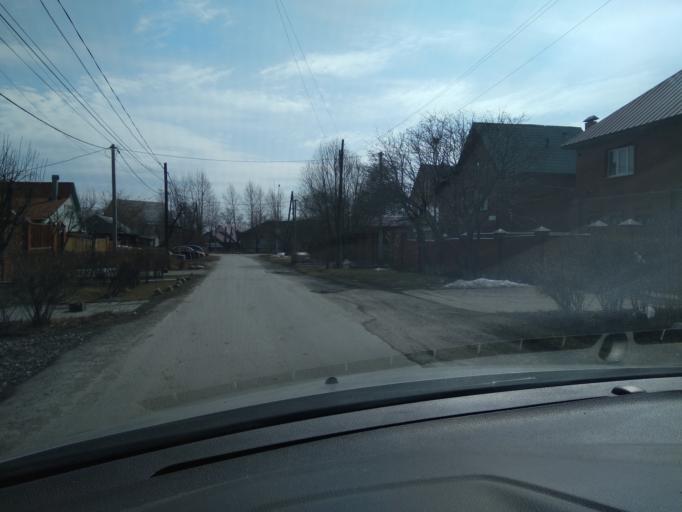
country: RU
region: Sverdlovsk
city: Shuvakish
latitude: 56.8881
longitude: 60.4857
